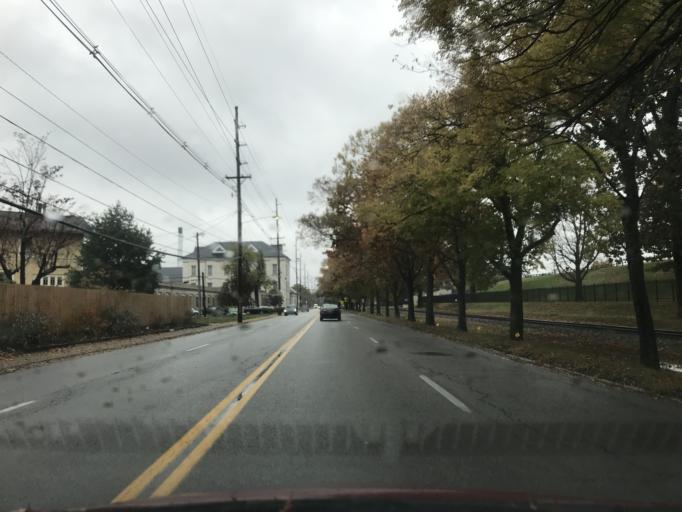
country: US
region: Kentucky
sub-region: Jefferson County
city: Saint Matthews
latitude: 38.2545
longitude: -85.6784
